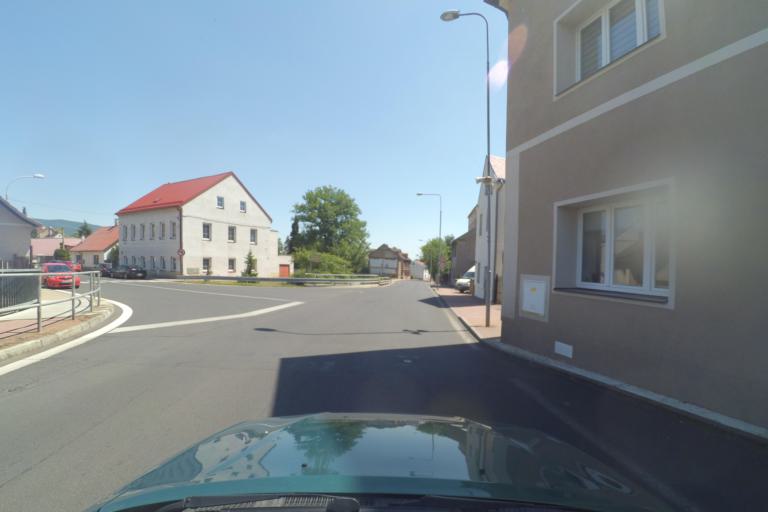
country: CZ
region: Ustecky
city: Novosedlice
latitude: 50.6693
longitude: 13.8033
